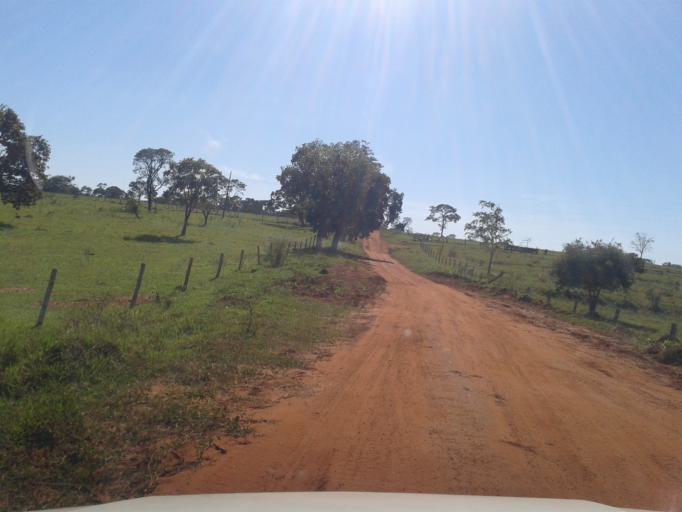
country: BR
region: Minas Gerais
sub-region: Ituiutaba
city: Ituiutaba
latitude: -19.1073
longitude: -49.8191
